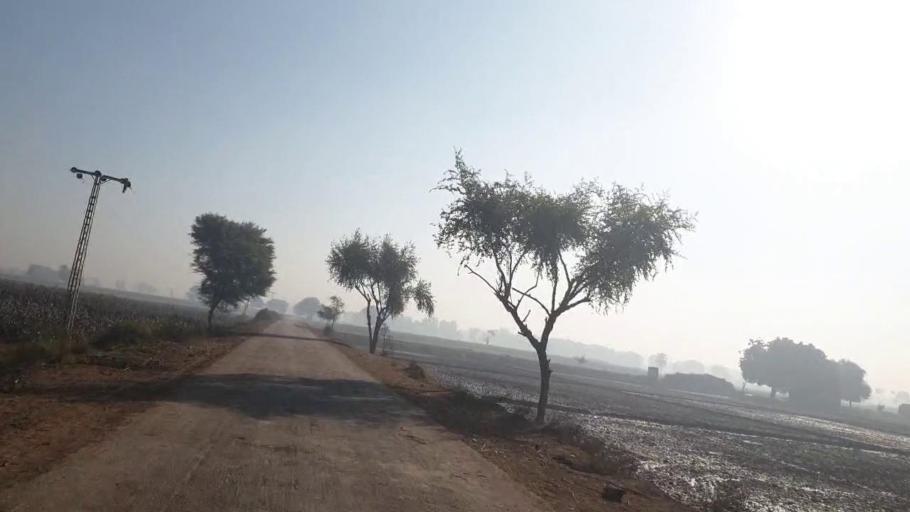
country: PK
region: Sindh
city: Dadu
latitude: 26.6749
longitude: 67.7954
